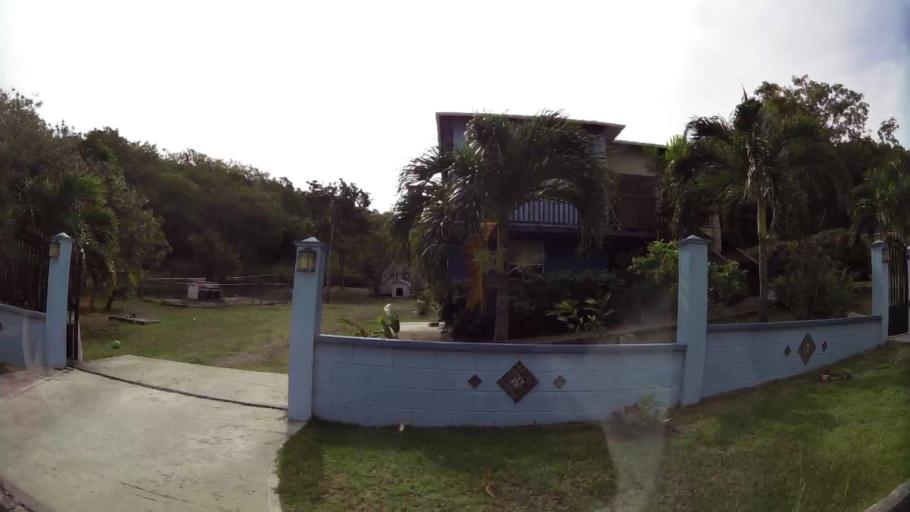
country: AG
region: Saint Peter
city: Parham
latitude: 17.0577
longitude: -61.7281
